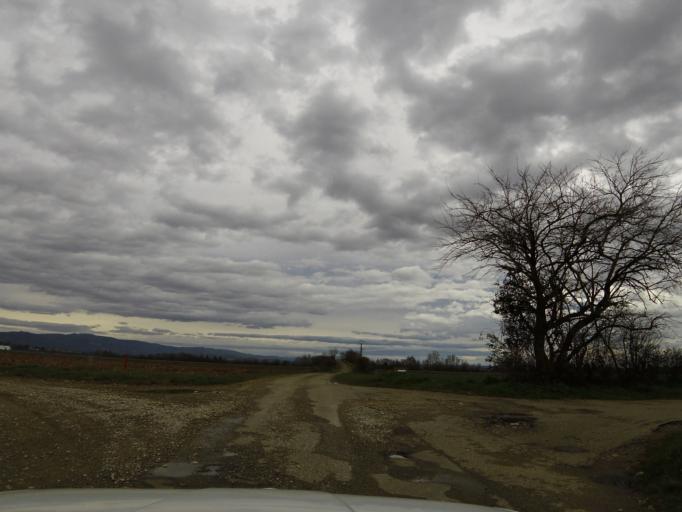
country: FR
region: Rhone-Alpes
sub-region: Departement de l'Ain
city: Meximieux
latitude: 45.8944
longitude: 5.2128
